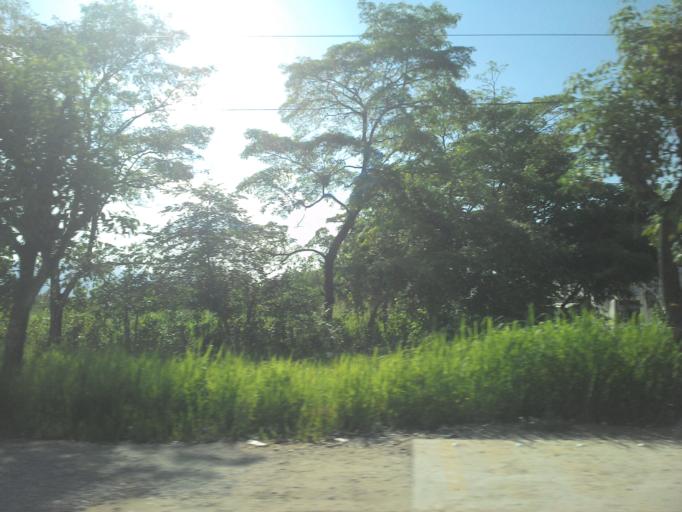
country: MX
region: Chiapas
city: Palenque
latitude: 17.5379
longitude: -91.9915
